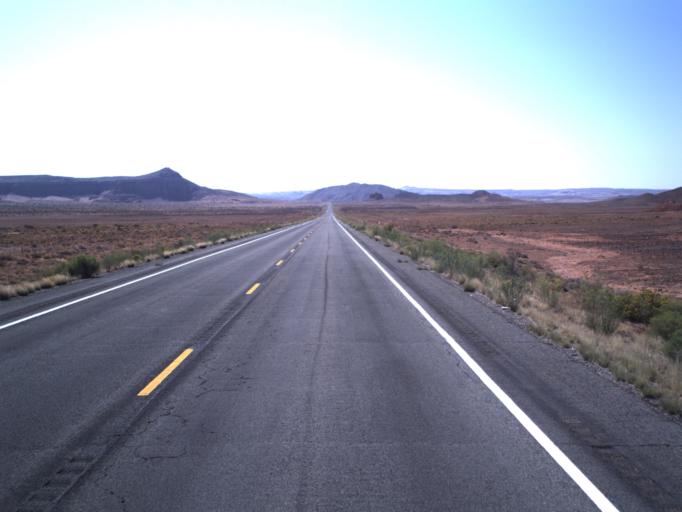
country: US
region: Utah
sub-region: San Juan County
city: Blanding
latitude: 37.0096
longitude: -109.6119
